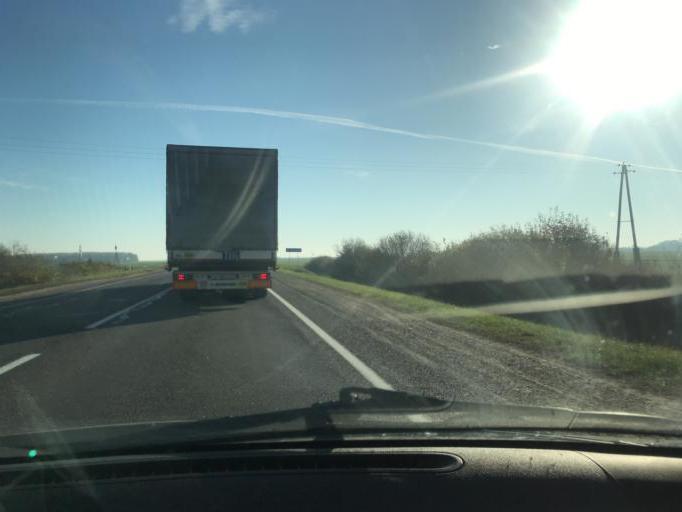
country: BY
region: Brest
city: Ivanava
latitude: 52.1472
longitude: 25.4416
